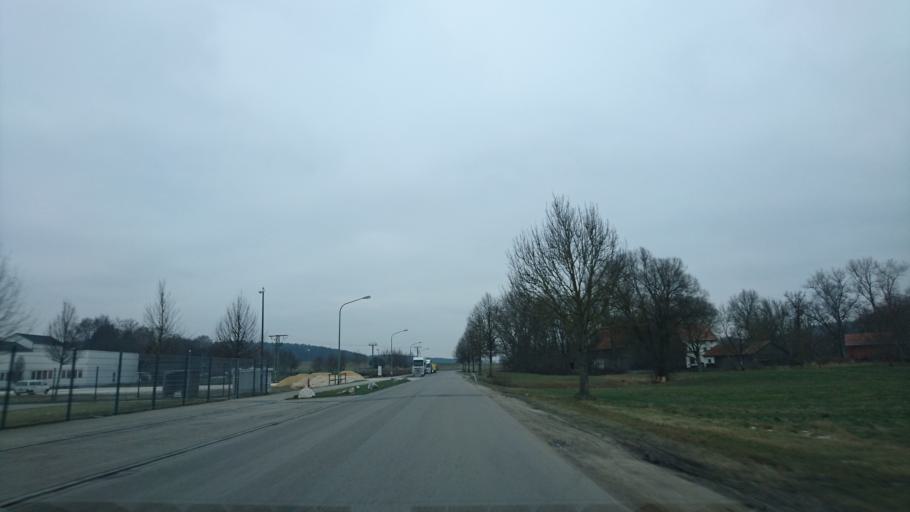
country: DE
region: Bavaria
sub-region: Swabia
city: Zusmarshausen
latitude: 48.4158
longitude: 10.5923
